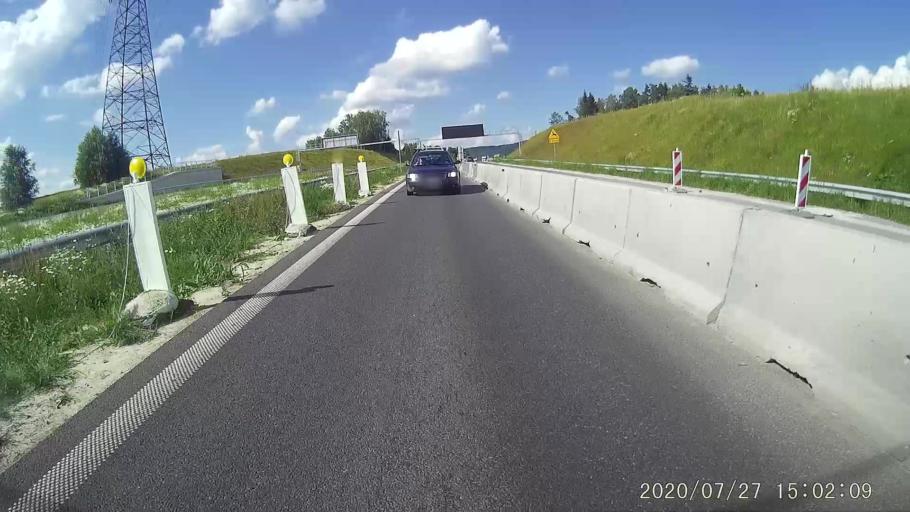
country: PL
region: Lesser Poland Voivodeship
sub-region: Powiat suski
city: Letownia
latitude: 49.6745
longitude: 19.8879
